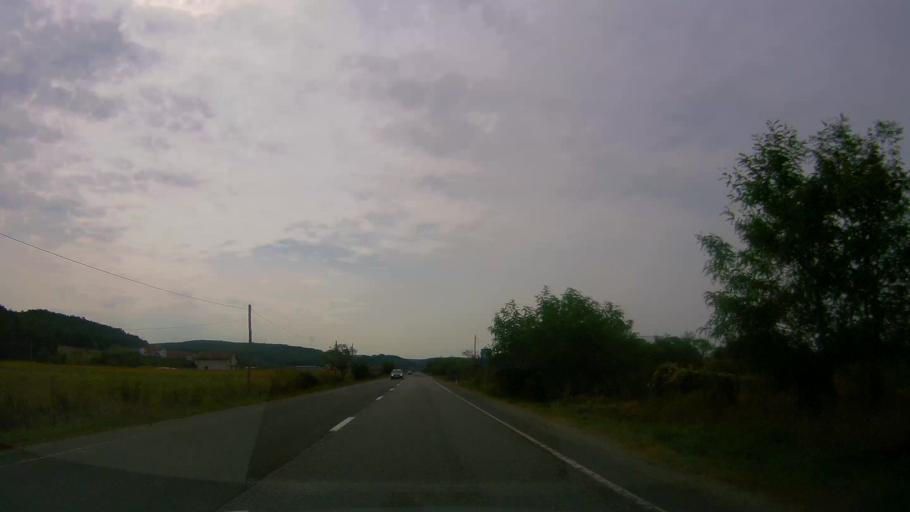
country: RO
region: Salaj
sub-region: Comuna Romanasi
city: Romanasi
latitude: 47.1053
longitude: 23.1862
